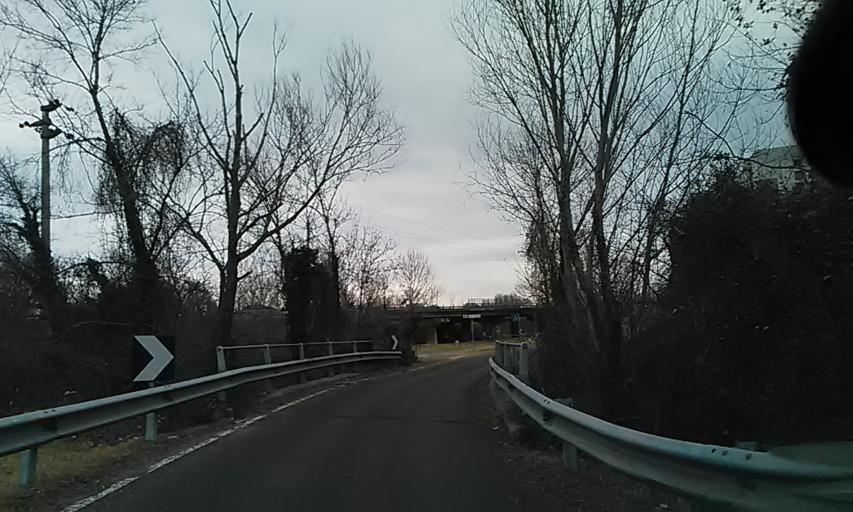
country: IT
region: Piedmont
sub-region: Provincia di Torino
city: Ivrea
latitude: 45.4647
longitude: 7.8868
